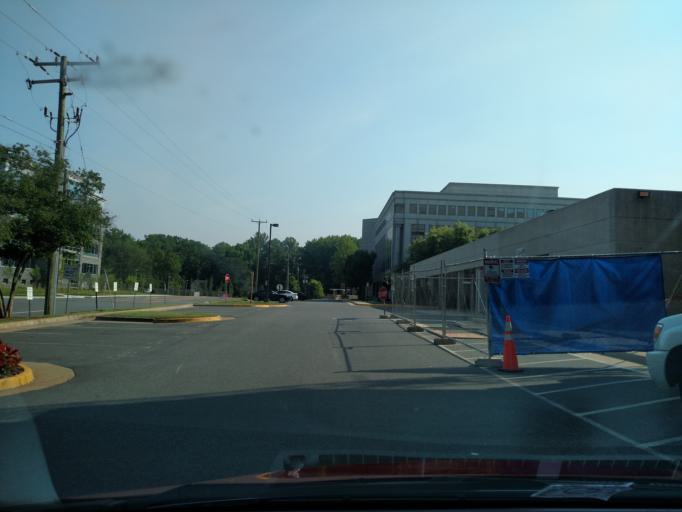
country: US
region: Virginia
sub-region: Fairfax County
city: Merrifield
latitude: 38.8647
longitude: -77.2345
